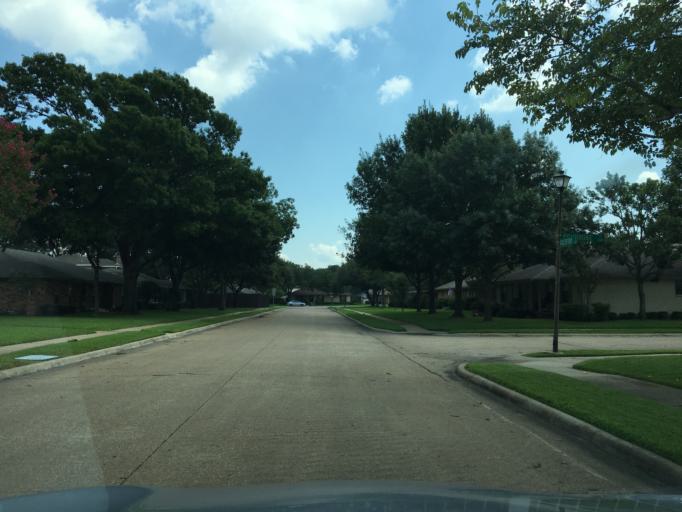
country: US
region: Texas
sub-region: Dallas County
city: Garland
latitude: 32.9373
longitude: -96.6456
